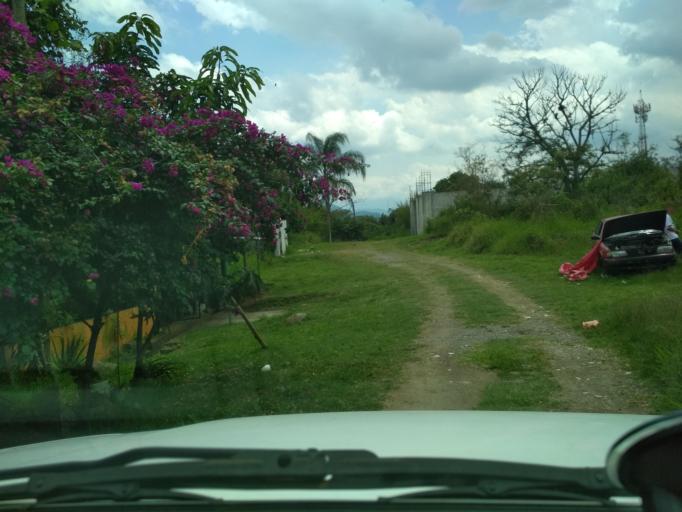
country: MX
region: Veracruz
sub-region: Cordoba
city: San Jose de Abajo [Unidad Habitacional]
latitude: 18.9209
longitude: -96.9657
